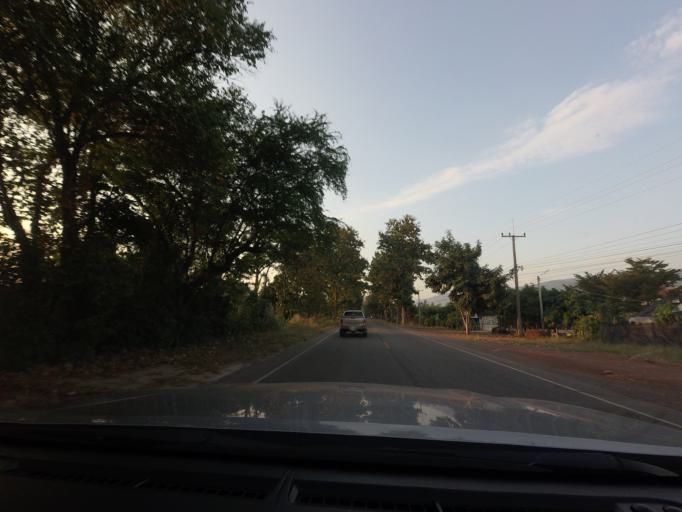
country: TH
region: Phitsanulok
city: Wang Thong
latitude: 16.6965
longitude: 100.5193
